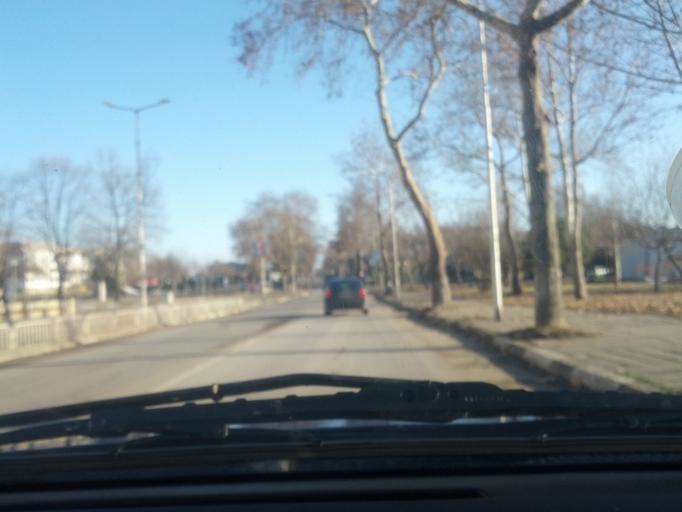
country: BG
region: Vratsa
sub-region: Obshtina Kozloduy
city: Kozloduy
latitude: 43.7766
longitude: 23.7314
